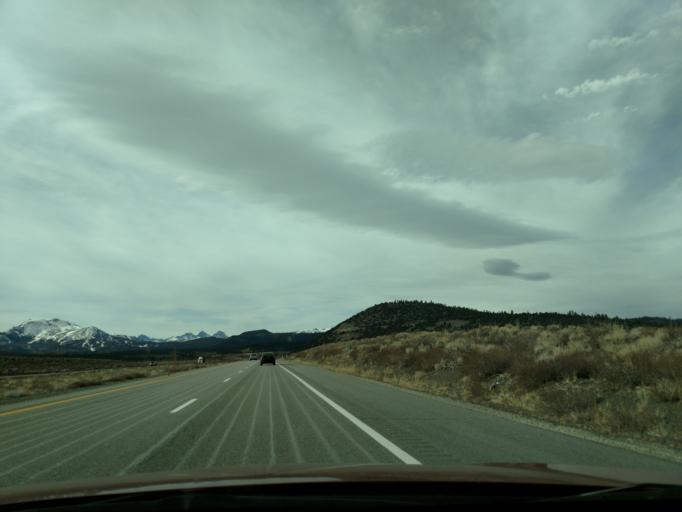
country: US
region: California
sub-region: Mono County
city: Mammoth Lakes
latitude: 37.6320
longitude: -118.8734
